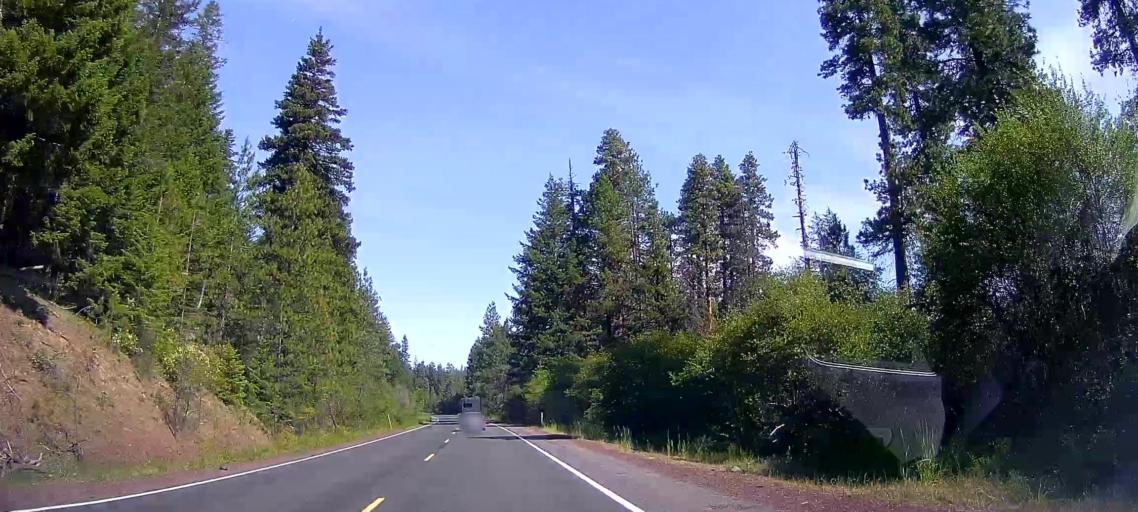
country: US
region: Oregon
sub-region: Jefferson County
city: Warm Springs
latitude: 45.0541
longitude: -121.5122
